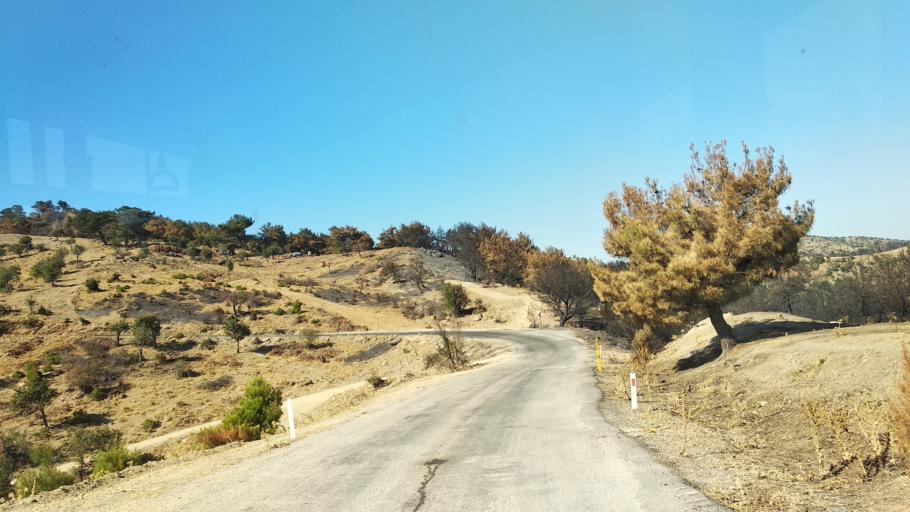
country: TR
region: Izmir
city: Gaziemir
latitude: 38.2940
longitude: 27.0014
